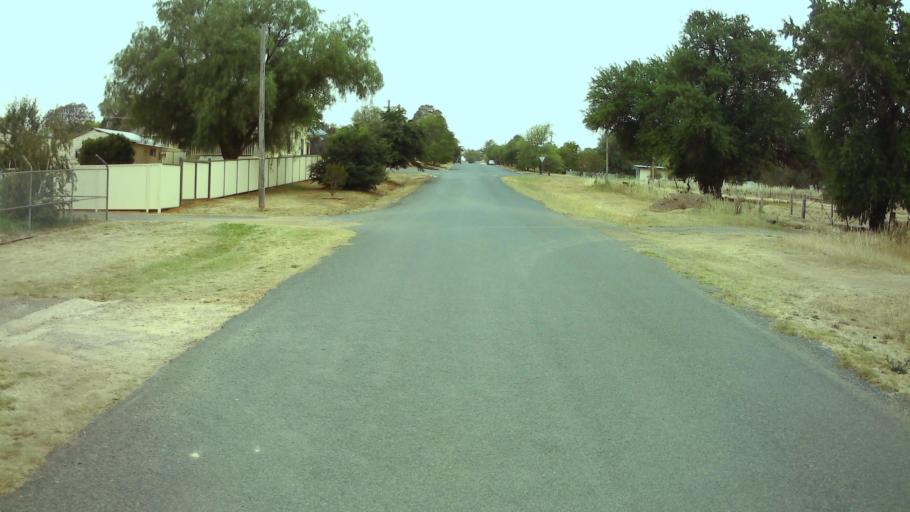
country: AU
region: New South Wales
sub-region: Weddin
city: Grenfell
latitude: -33.8992
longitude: 148.1558
